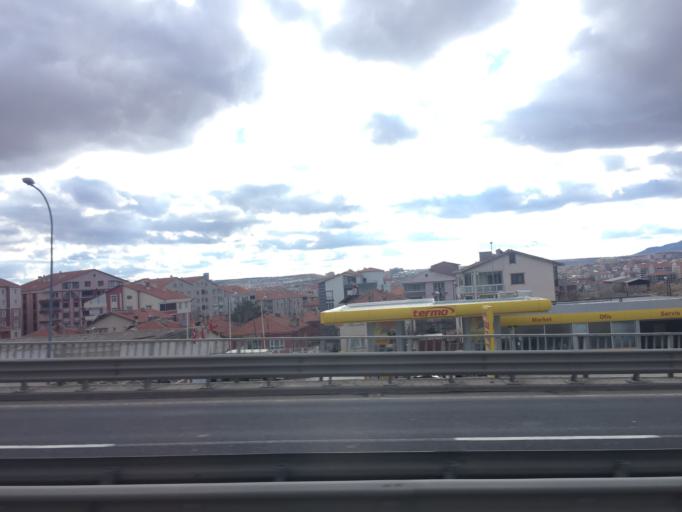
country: TR
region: Kirsehir
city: Kirsehir
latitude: 39.1600
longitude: 34.1602
